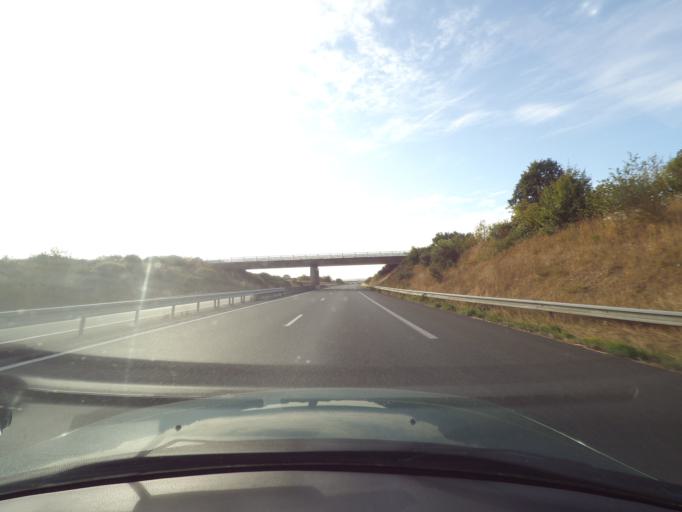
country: FR
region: Poitou-Charentes
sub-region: Departement des Deux-Sevres
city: Combrand
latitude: 46.9242
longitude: -0.7061
